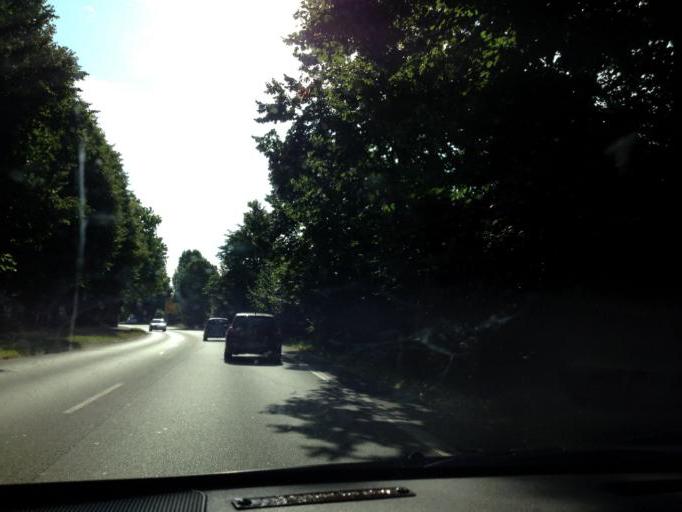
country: DE
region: North Rhine-Westphalia
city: Schwerte
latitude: 51.4817
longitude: 7.5195
